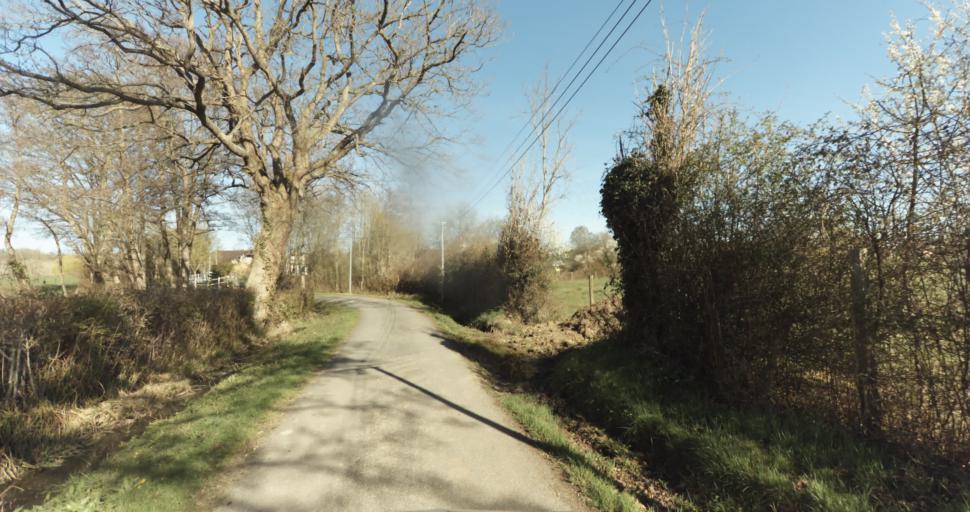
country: FR
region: Lower Normandy
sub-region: Departement du Calvados
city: Livarot
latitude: 49.0210
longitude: 0.0654
